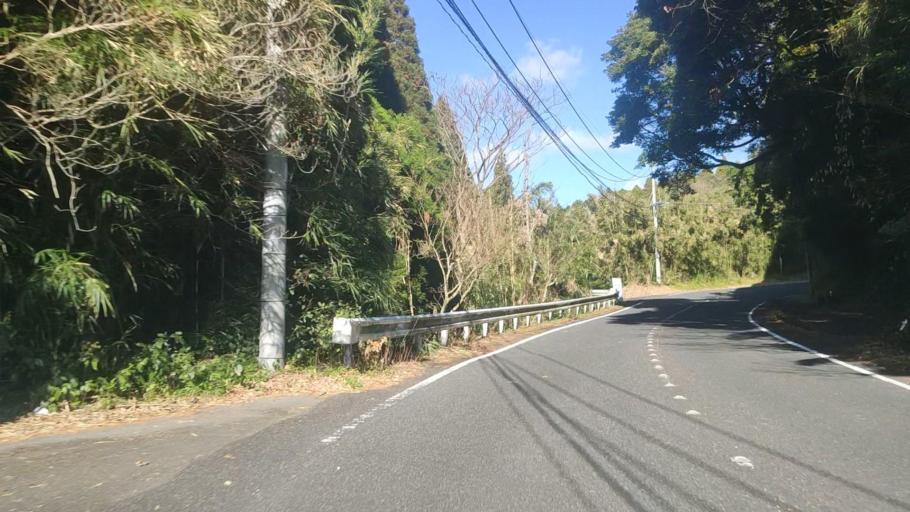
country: JP
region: Kagoshima
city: Kokubu-matsuki
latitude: 31.6712
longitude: 130.8299
